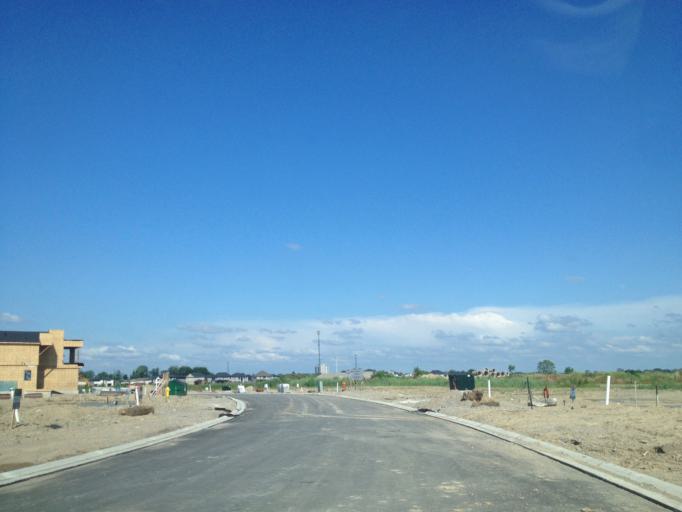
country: CA
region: Ontario
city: London
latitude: 43.0203
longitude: -81.3318
